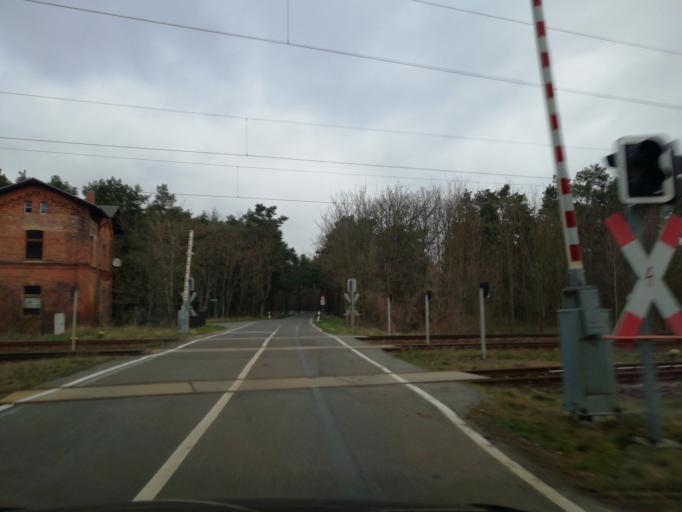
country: DE
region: Brandenburg
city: Vetschau
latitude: 51.7485
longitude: 14.1324
